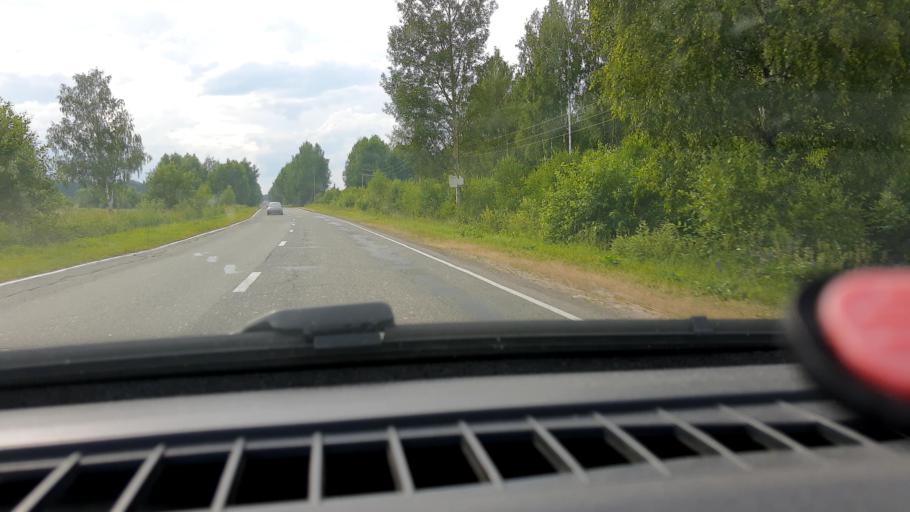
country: RU
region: Nizjnij Novgorod
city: Neklyudovo
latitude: 56.5096
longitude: 43.9605
